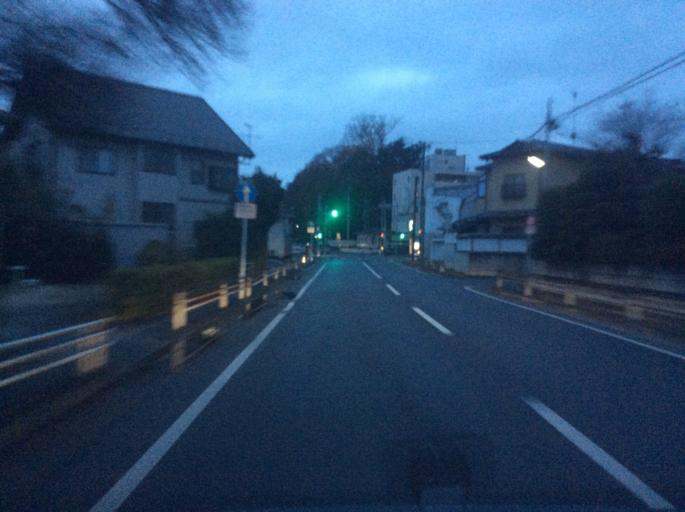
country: JP
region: Fukushima
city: Iwaki
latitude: 37.0628
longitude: 140.8945
